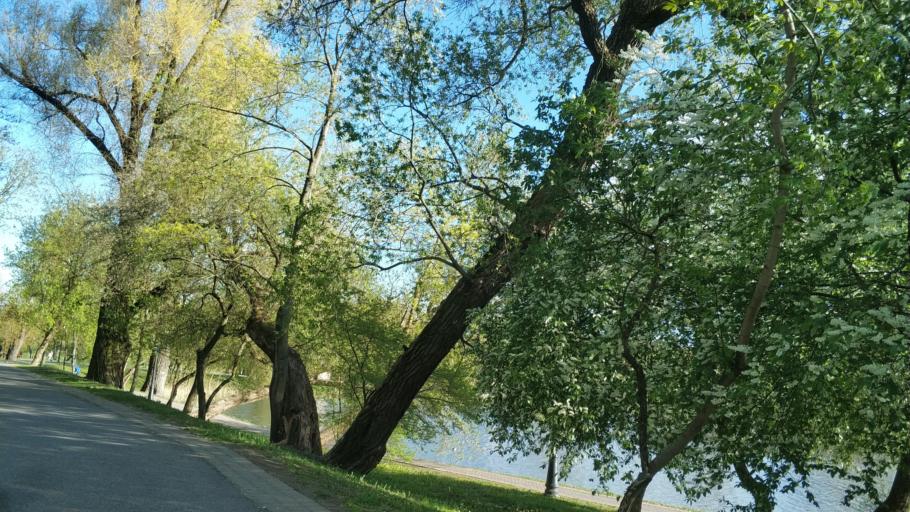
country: BY
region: Minsk
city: Syenitsa
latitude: 53.8513
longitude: 27.5767
